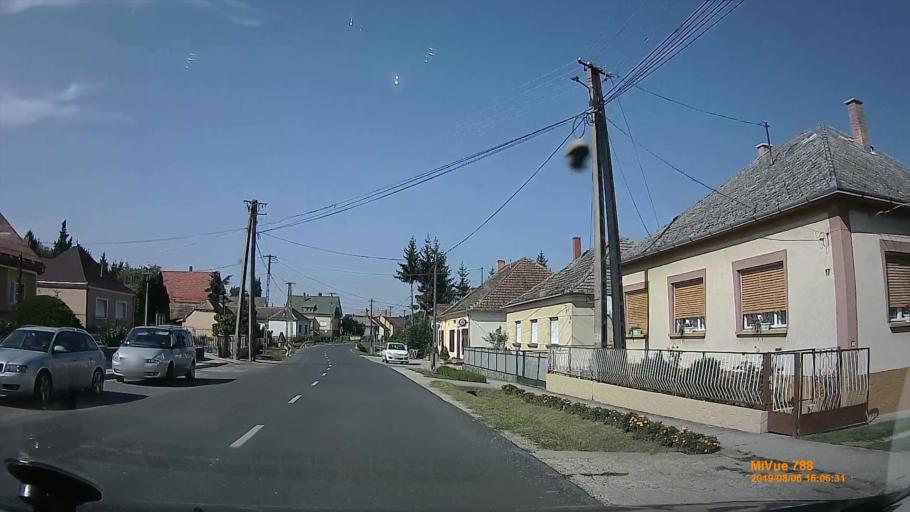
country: HU
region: Zala
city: Murakeresztur
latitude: 46.3206
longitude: 16.9696
